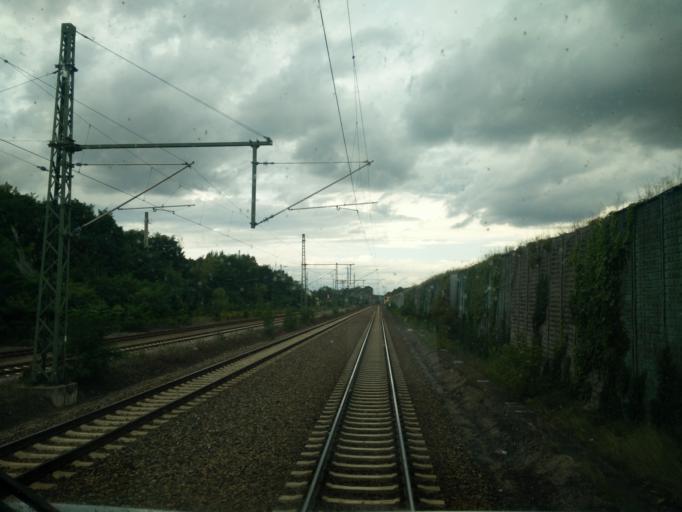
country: DE
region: Brandenburg
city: Luebben
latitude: 51.9415
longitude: 13.8744
